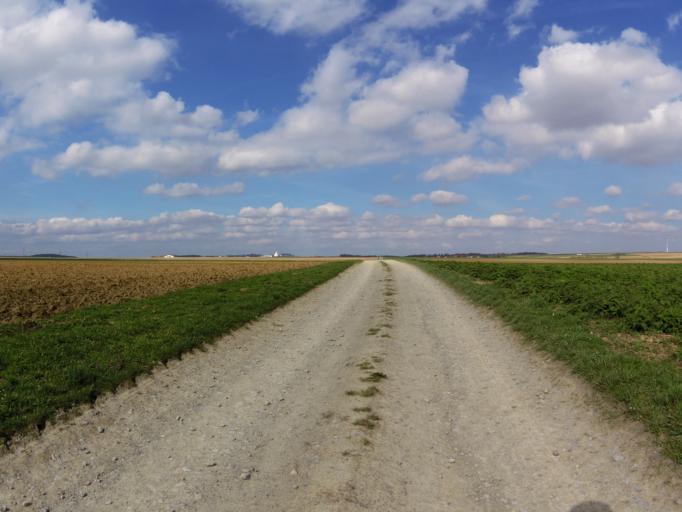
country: DE
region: Bavaria
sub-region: Regierungsbezirk Unterfranken
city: Biebelried
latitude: 49.7501
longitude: 10.0884
